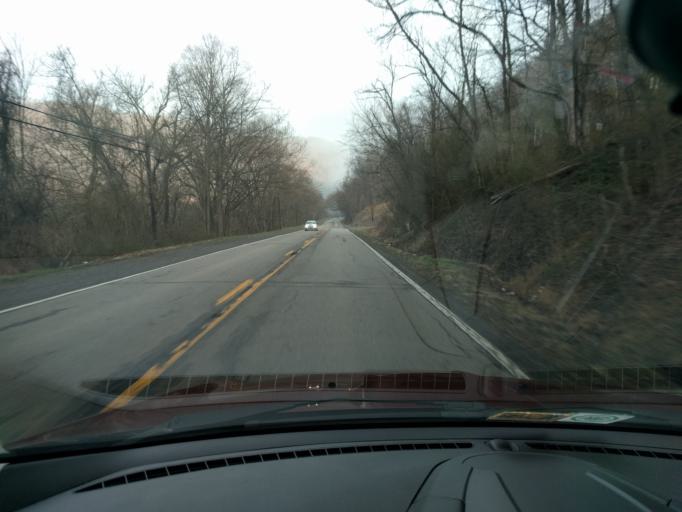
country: US
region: West Virginia
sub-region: Kanawha County
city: Montgomery
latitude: 38.1577
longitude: -81.2950
